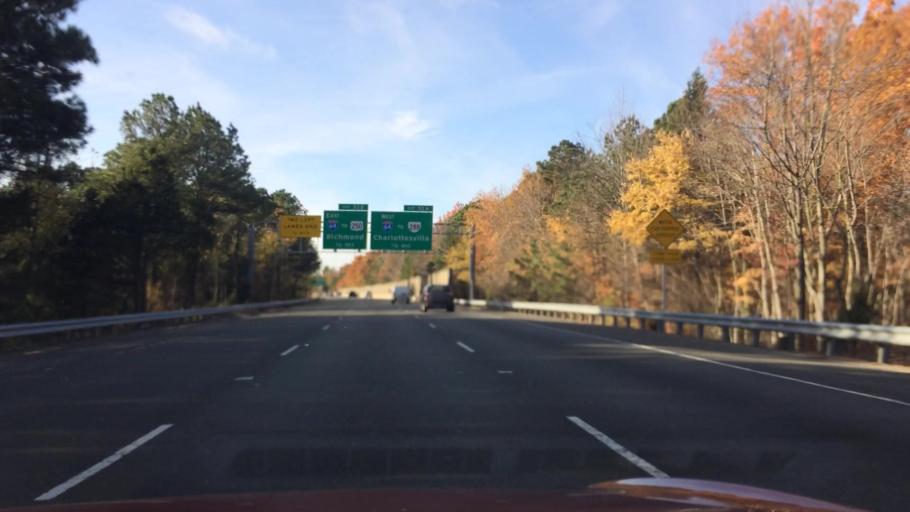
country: US
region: Virginia
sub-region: Henrico County
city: Short Pump
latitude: 37.6651
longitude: -77.5949
